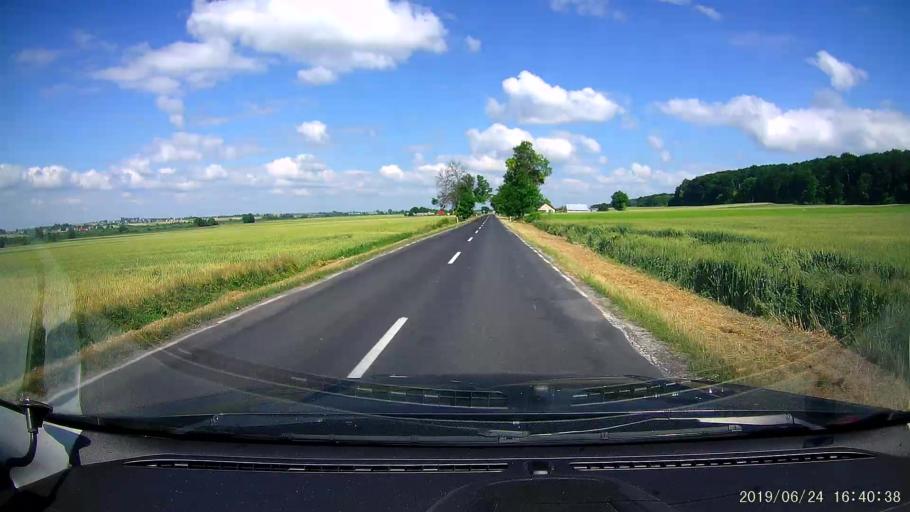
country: PL
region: Lublin Voivodeship
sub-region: Powiat tomaszowski
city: Michalow
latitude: 50.5305
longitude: 23.5774
